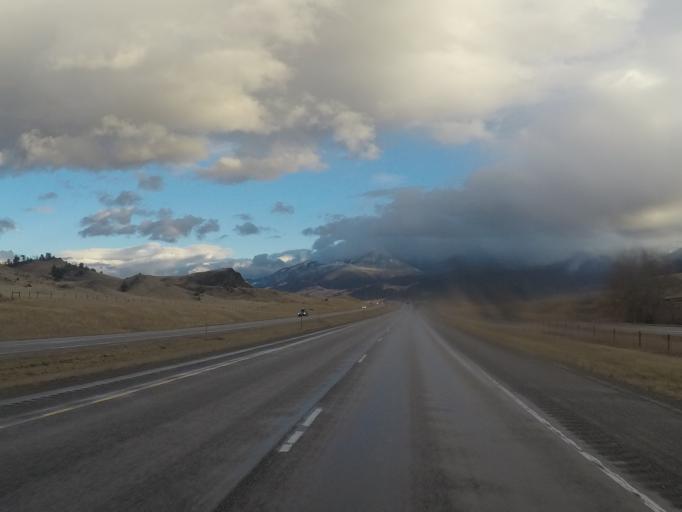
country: US
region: Montana
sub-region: Park County
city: Livingston
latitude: 45.6607
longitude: -110.6382
